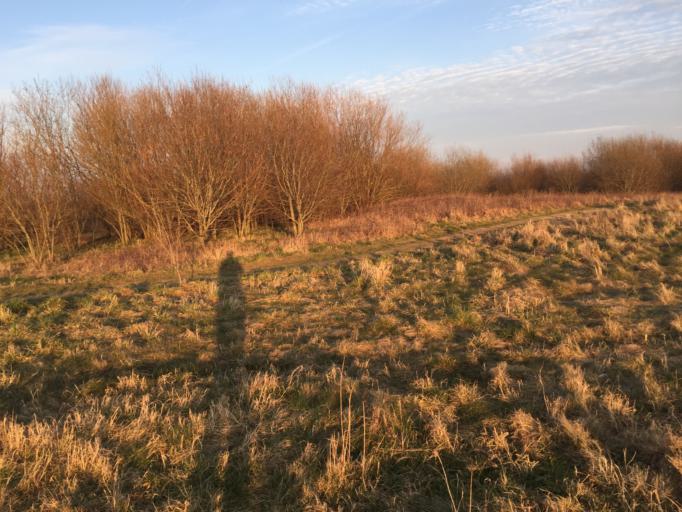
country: DK
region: South Denmark
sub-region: Kerteminde Kommune
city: Langeskov
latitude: 55.3319
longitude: 10.5240
